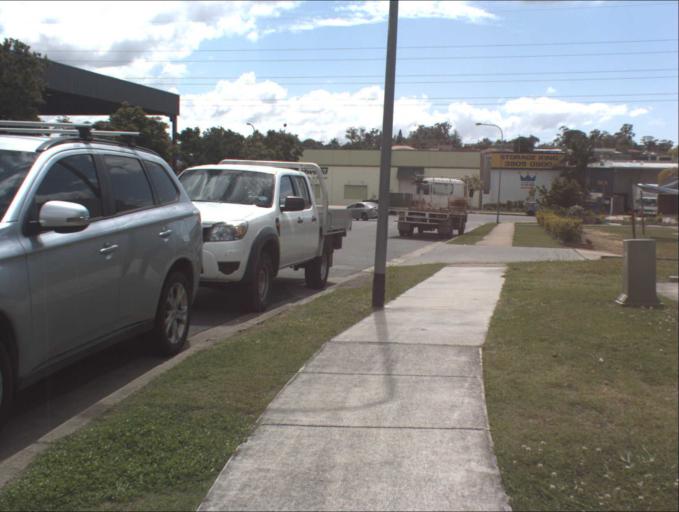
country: AU
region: Queensland
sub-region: Brisbane
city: Sunnybank Hills
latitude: -27.6650
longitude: 153.0474
